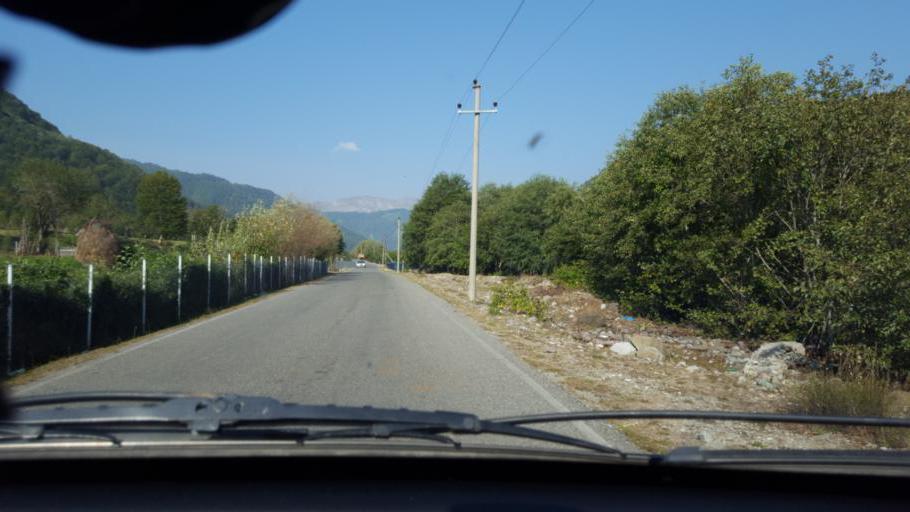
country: ME
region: Andrijevica
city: Andrijevica
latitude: 42.5883
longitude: 19.7101
